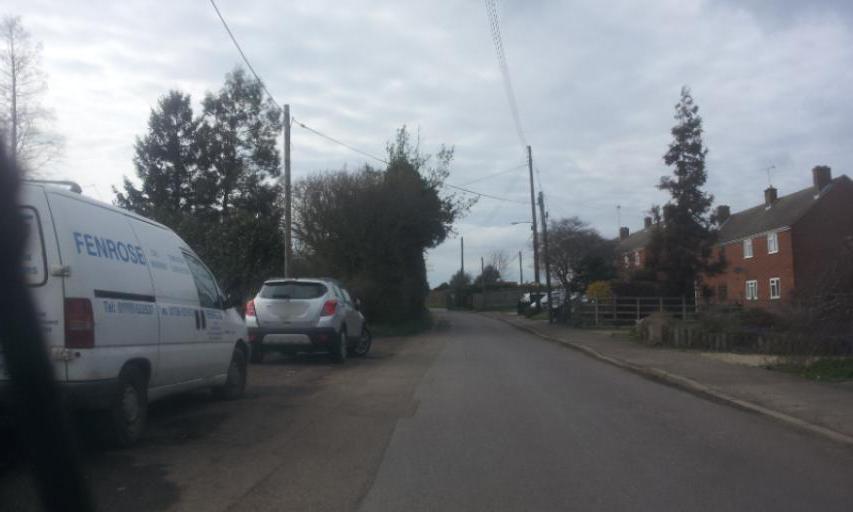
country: GB
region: England
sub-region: Kent
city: Teynham
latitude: 51.3270
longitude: 0.8285
